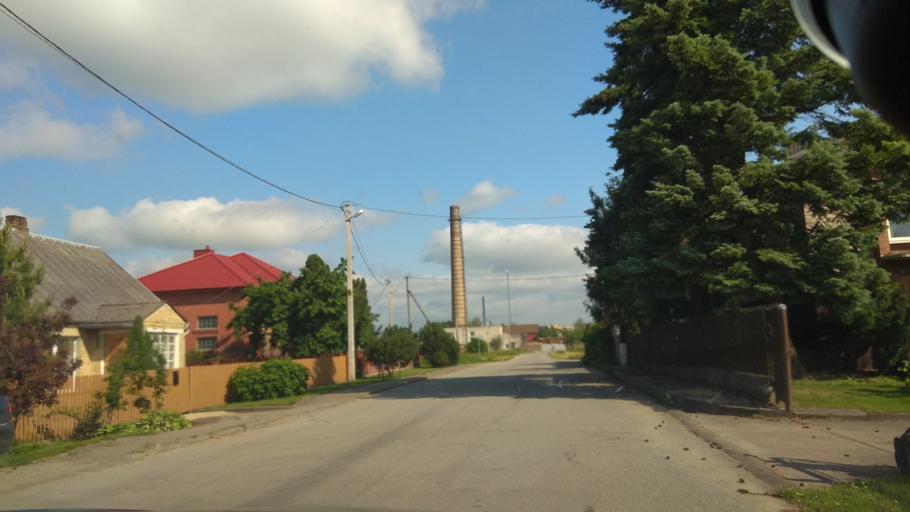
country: LT
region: Siauliu apskritis
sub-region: Joniskis
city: Joniskis
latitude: 56.2450
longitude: 23.6259
